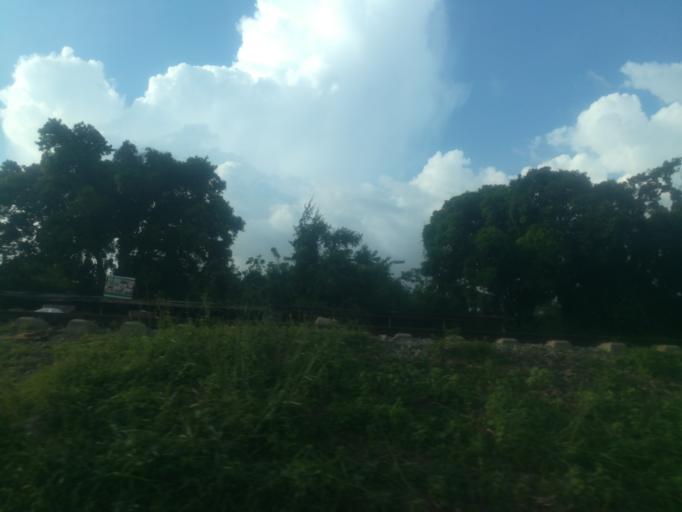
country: NG
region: Oyo
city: Ibadan
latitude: 7.3812
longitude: 3.8670
